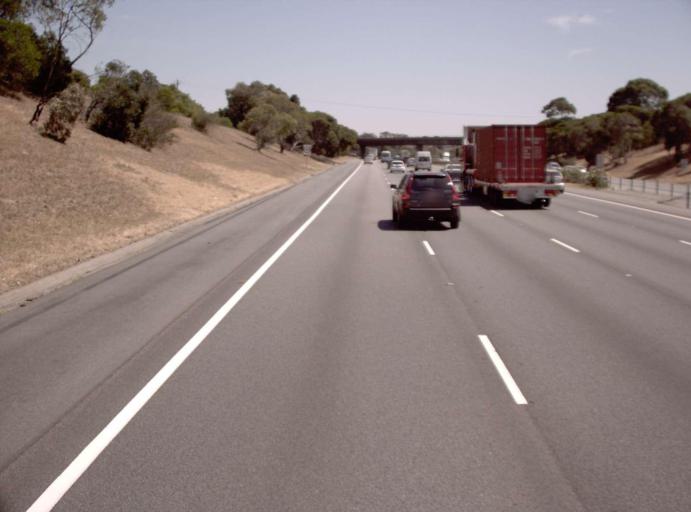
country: AU
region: Victoria
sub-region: Monash
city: Notting Hill
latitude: -37.9071
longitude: 145.1580
